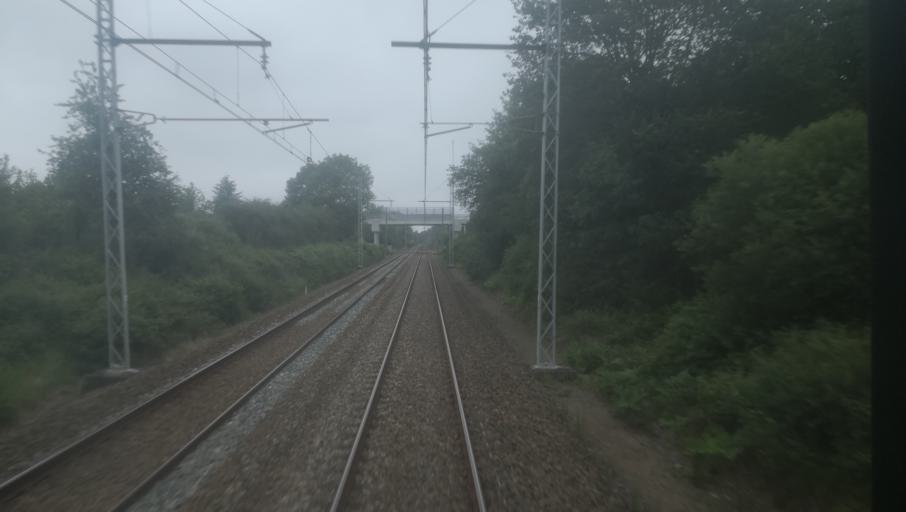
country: FR
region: Centre
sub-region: Departement de l'Indre
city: Luant
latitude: 46.6817
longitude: 1.5529
